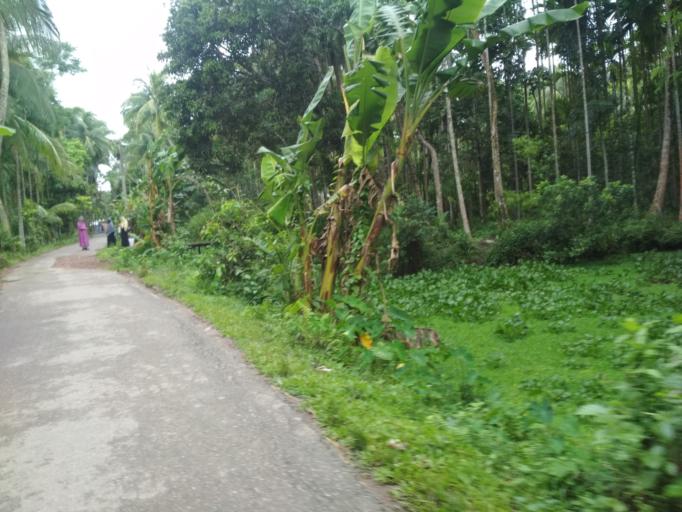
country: BD
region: Chittagong
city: Lakshmipur
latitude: 22.9675
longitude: 90.7961
